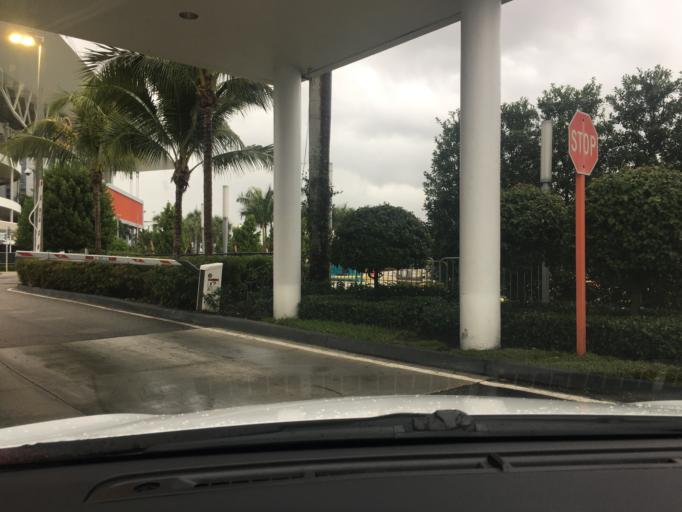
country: US
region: Florida
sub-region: Miami-Dade County
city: Lake Lucerne
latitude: 25.9557
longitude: -80.2383
